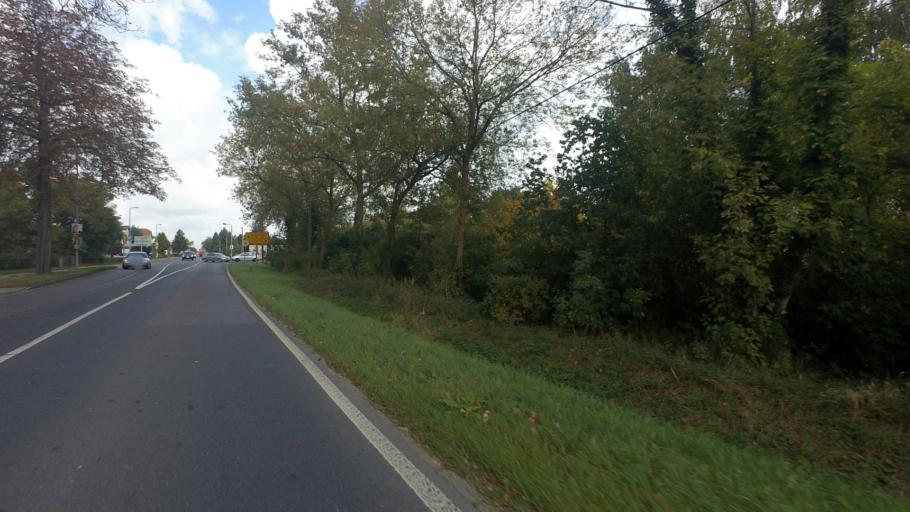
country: DE
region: Brandenburg
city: Herzberg
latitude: 51.6914
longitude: 13.2529
